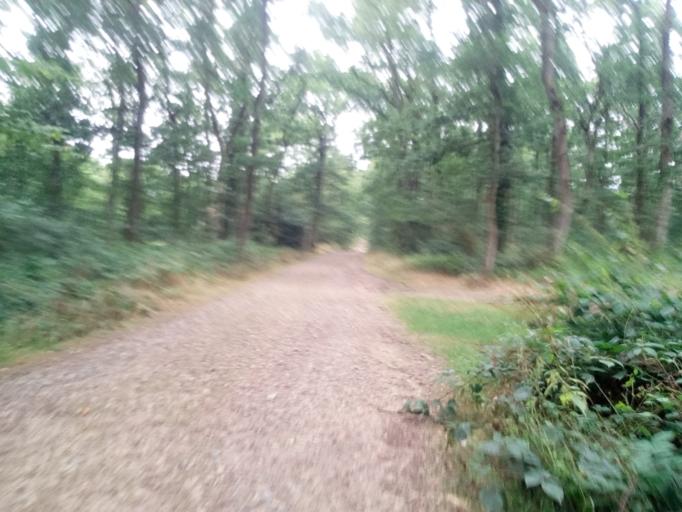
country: FR
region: Lower Normandy
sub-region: Departement du Calvados
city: Clinchamps-sur-Orne
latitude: 49.0482
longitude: -0.4340
